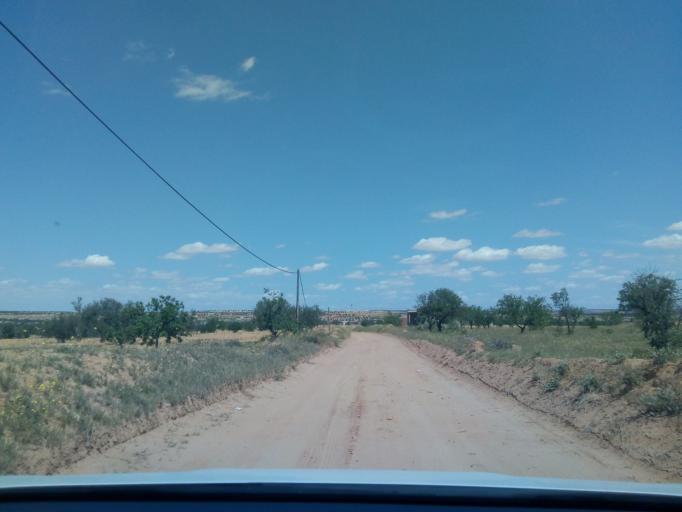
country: TN
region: Safaqis
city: Sfax
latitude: 34.7290
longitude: 10.4866
